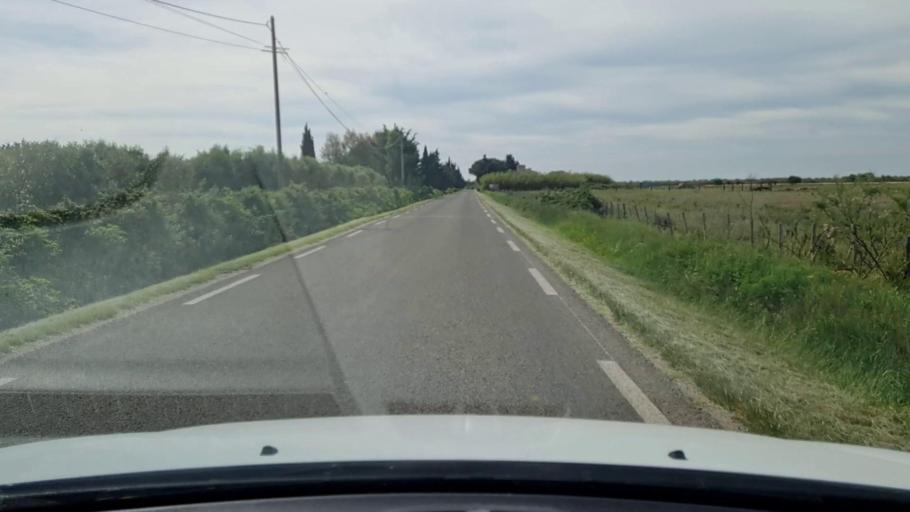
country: FR
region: Languedoc-Roussillon
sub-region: Departement de l'Herault
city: Marsillargues
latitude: 43.6196
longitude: 4.2036
